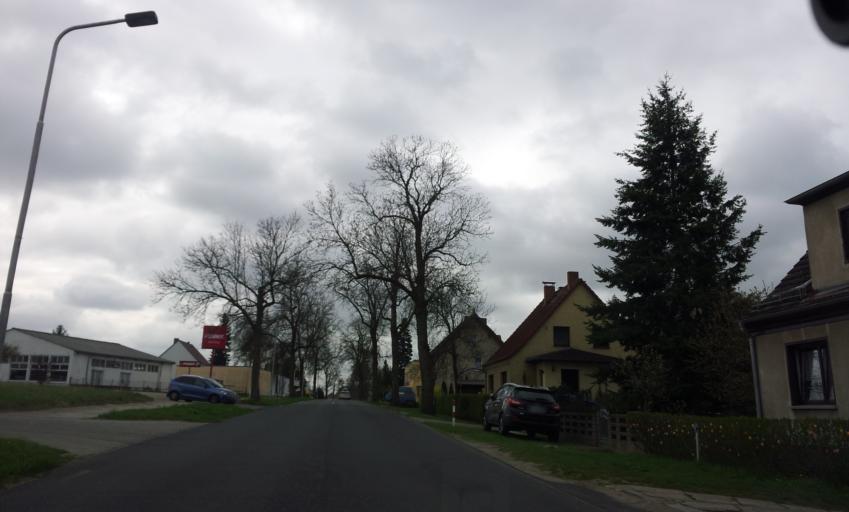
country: DE
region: Brandenburg
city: Juterbog
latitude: 51.9826
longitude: 13.1003
